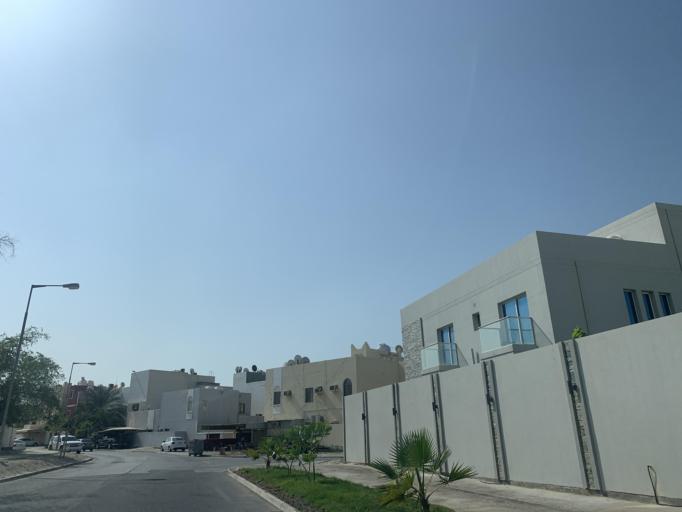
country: BH
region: Central Governorate
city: Madinat Hamad
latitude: 26.1293
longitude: 50.5014
